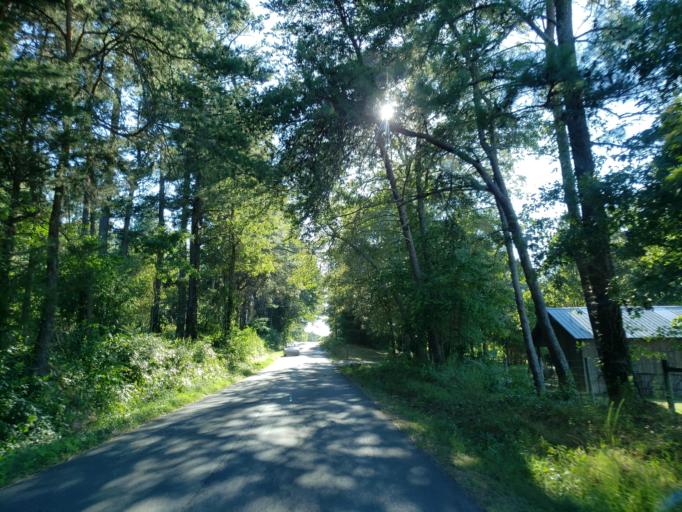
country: US
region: Georgia
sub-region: Polk County
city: Aragon
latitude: 34.1228
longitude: -85.0242
